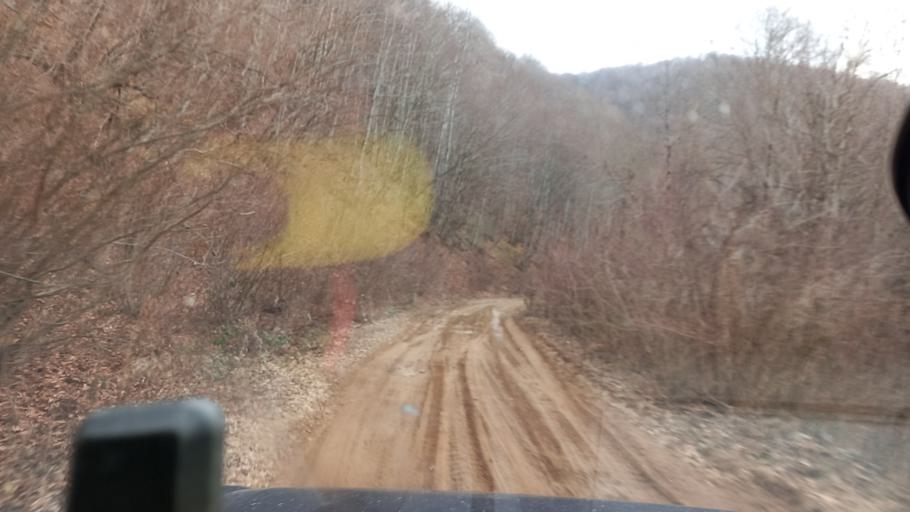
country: RU
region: Adygeya
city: Kamennomostskiy
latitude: 44.1769
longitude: 40.2989
